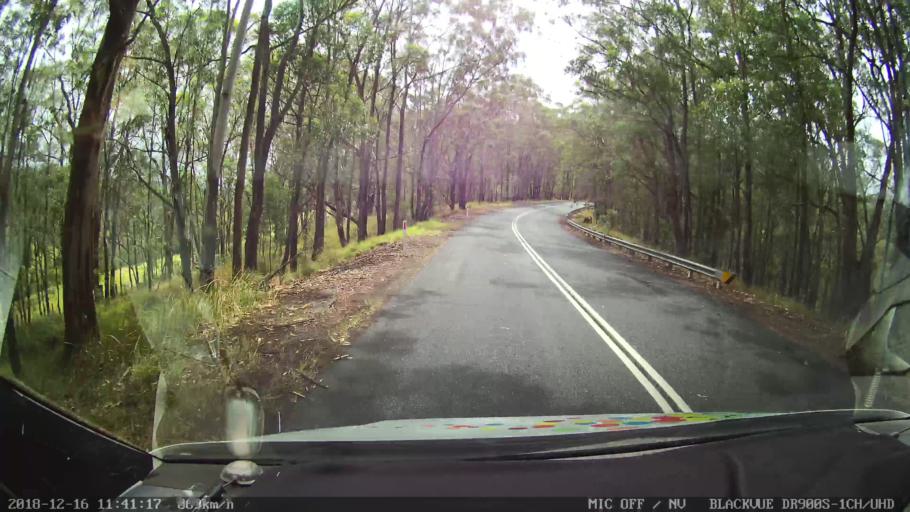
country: AU
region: New South Wales
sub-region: Tenterfield Municipality
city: Carrolls Creek
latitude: -28.9584
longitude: 152.2073
